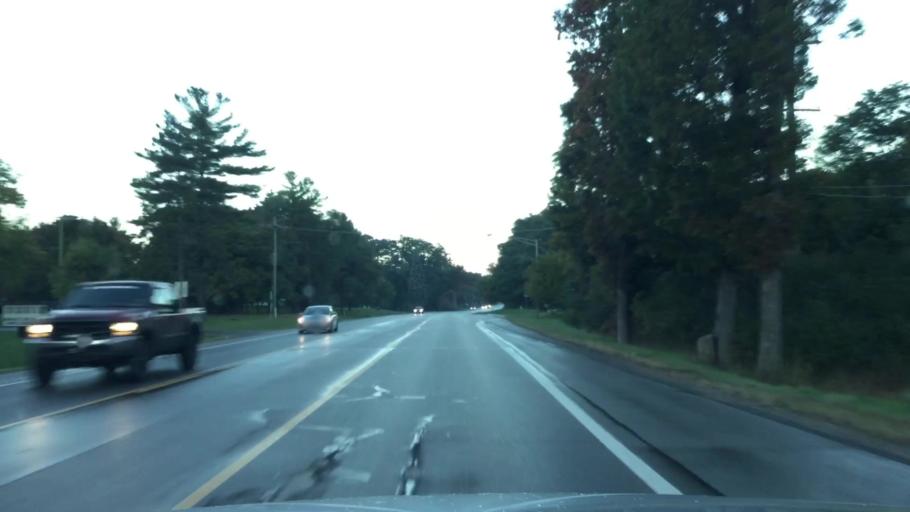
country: US
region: Michigan
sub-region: Livingston County
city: Howell
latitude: 42.6223
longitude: -83.9086
